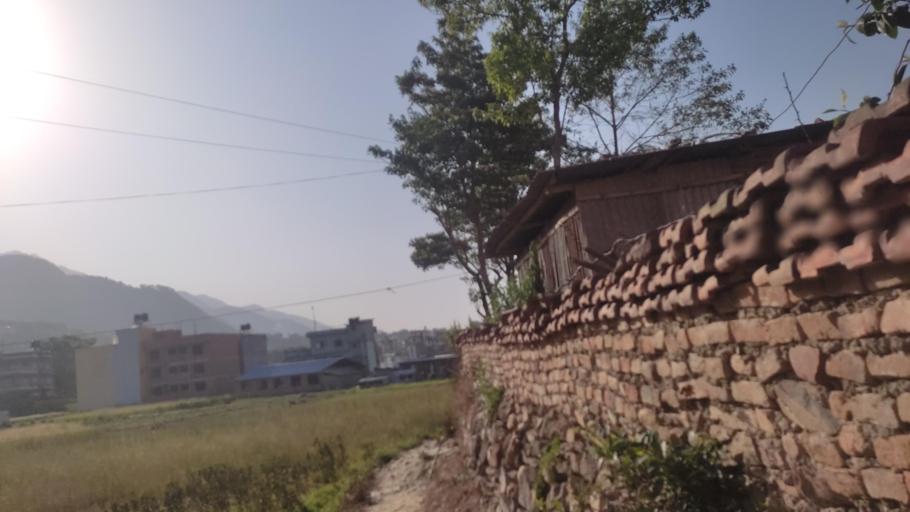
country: NP
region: Central Region
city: Kirtipur
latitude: 27.6597
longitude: 85.2702
